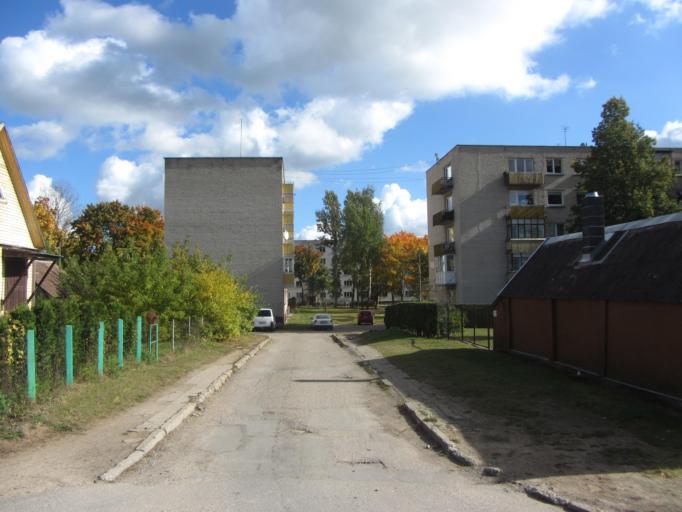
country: LT
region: Utenos apskritis
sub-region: Utena
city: Utena
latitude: 55.5029
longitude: 25.6133
